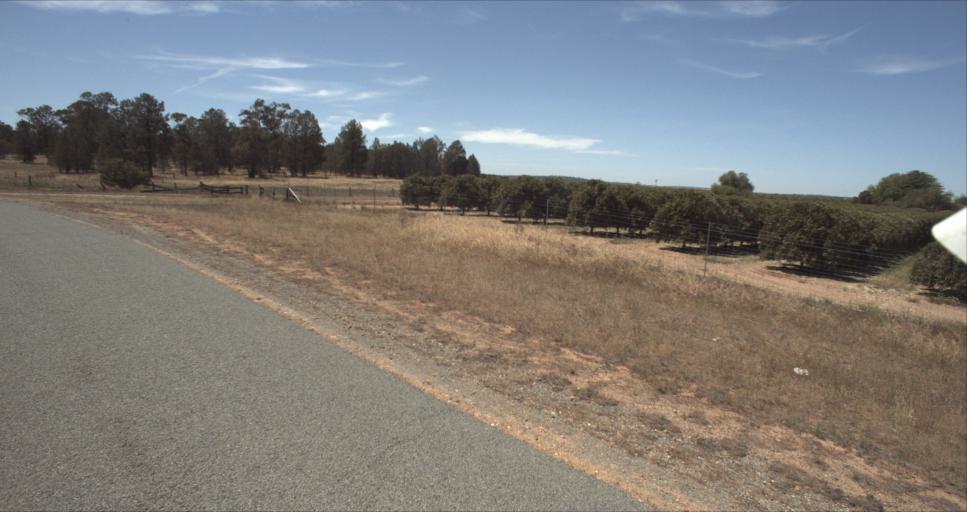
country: AU
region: New South Wales
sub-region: Leeton
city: Leeton
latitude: -34.6738
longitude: 146.4441
